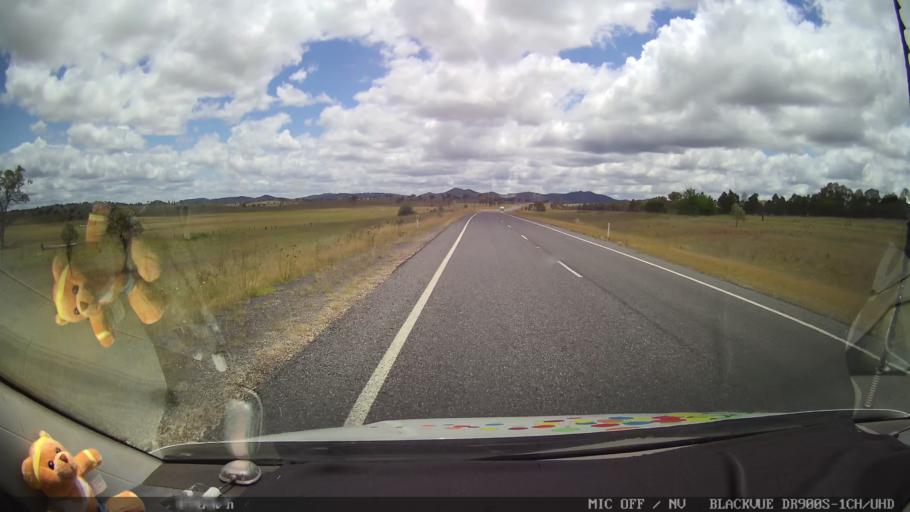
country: AU
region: New South Wales
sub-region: Glen Innes Severn
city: Glen Innes
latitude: -29.4026
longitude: 151.8728
